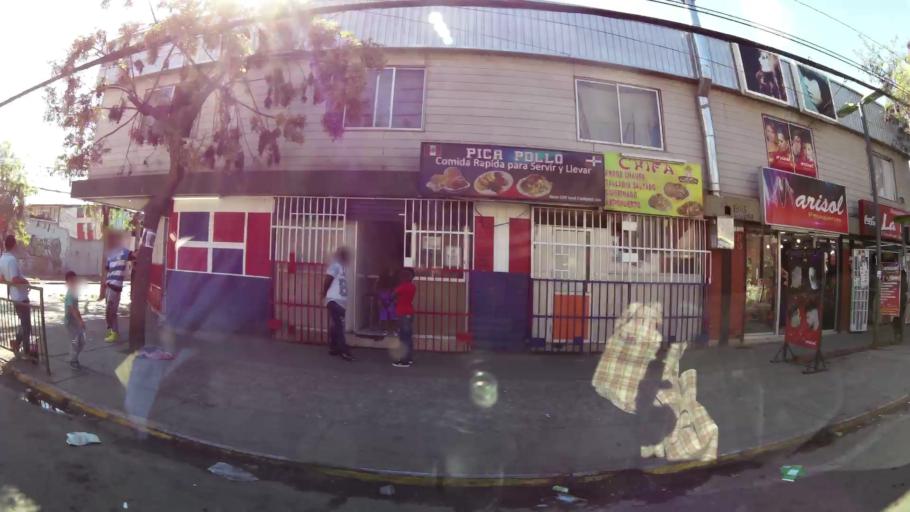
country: CL
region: Santiago Metropolitan
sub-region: Provincia de Santiago
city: Santiago
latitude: -33.4259
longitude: -70.6574
